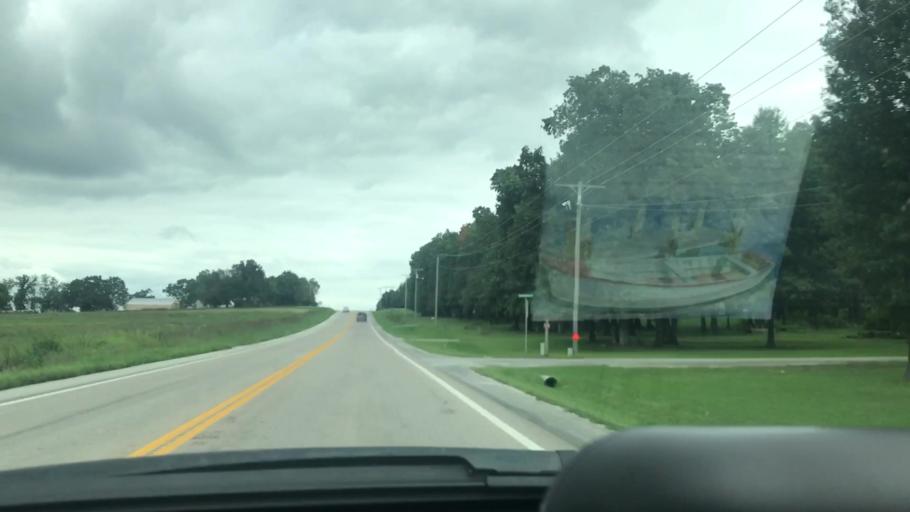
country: US
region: Missouri
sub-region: Dallas County
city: Buffalo
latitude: 37.6705
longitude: -93.1033
